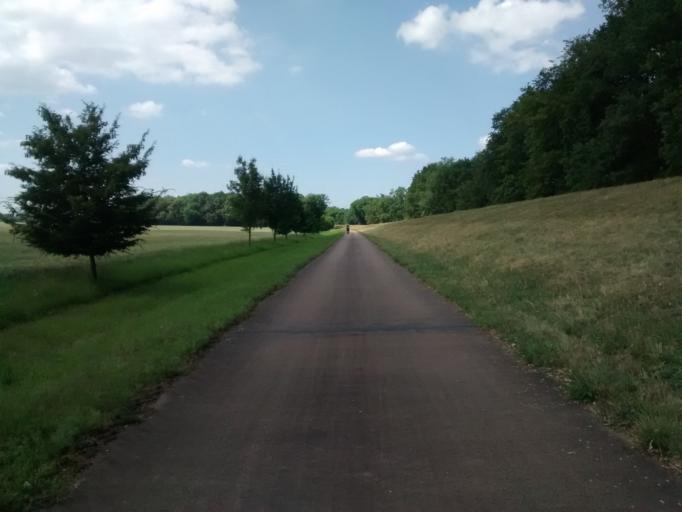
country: DE
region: Saxony-Anhalt
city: Bergwitz
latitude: 51.8495
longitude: 12.5278
